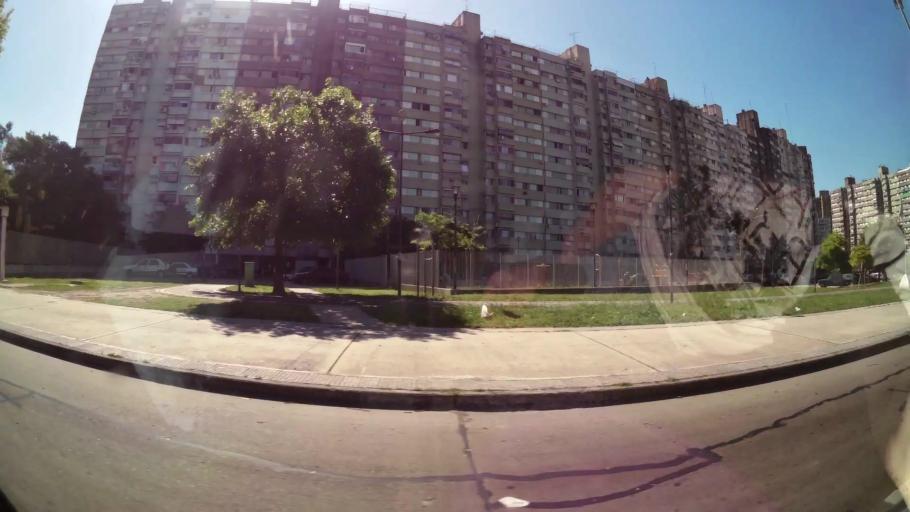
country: AR
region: Buenos Aires F.D.
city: Villa Lugano
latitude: -34.6900
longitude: -58.4618
